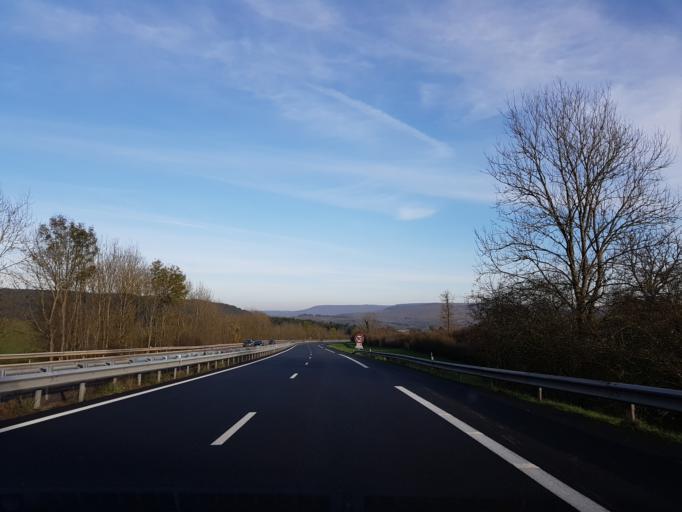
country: FR
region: Bourgogne
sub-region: Departement de la Cote-d'Or
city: Fleurey-sur-Ouche
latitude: 47.3054
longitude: 4.7514
